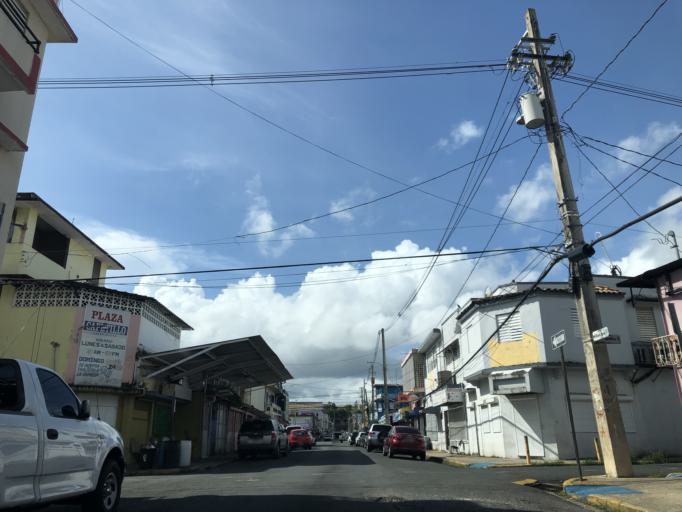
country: PR
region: Trujillo Alto
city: Trujillo Alto
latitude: 18.4010
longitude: -66.0460
